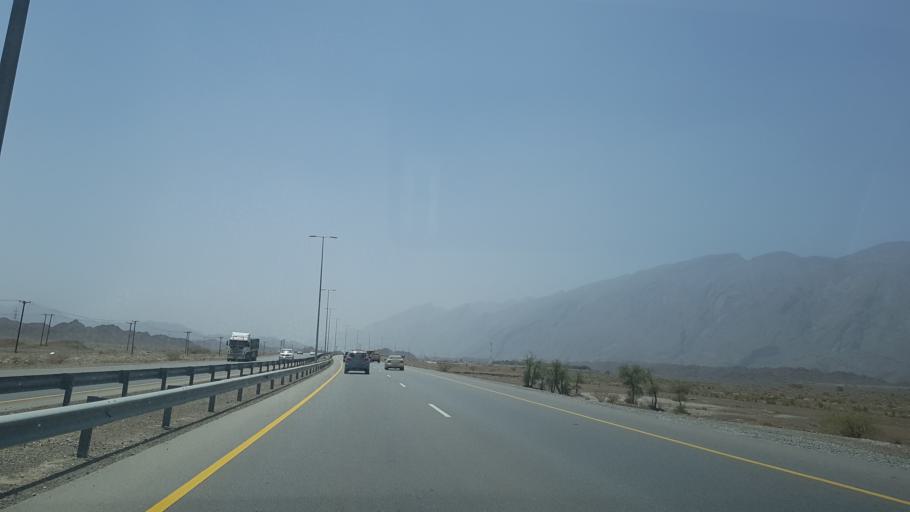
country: OM
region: Muhafazat ad Dakhiliyah
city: Sufalat Sama'il
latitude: 23.2572
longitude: 57.9300
